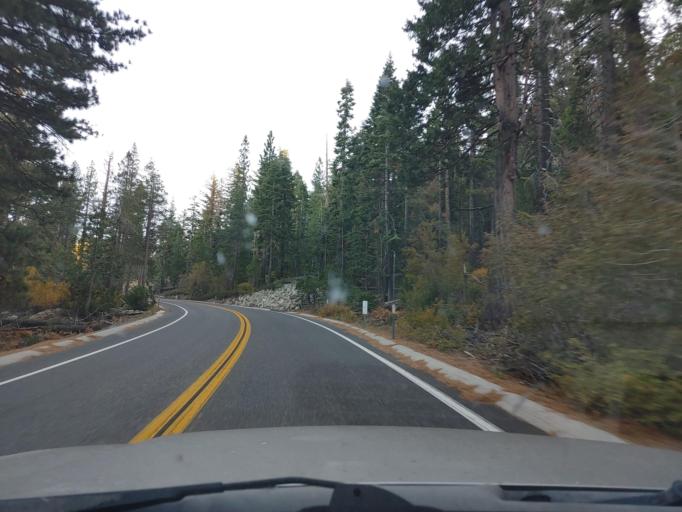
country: US
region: California
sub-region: Placer County
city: Tahoma
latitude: 38.9899
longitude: -120.1107
